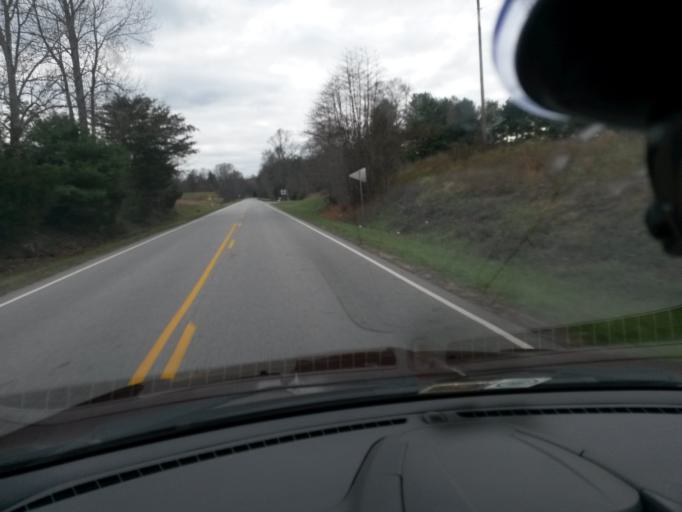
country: US
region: Virginia
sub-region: City of Lynchburg
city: West Lynchburg
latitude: 37.5440
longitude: -79.2850
